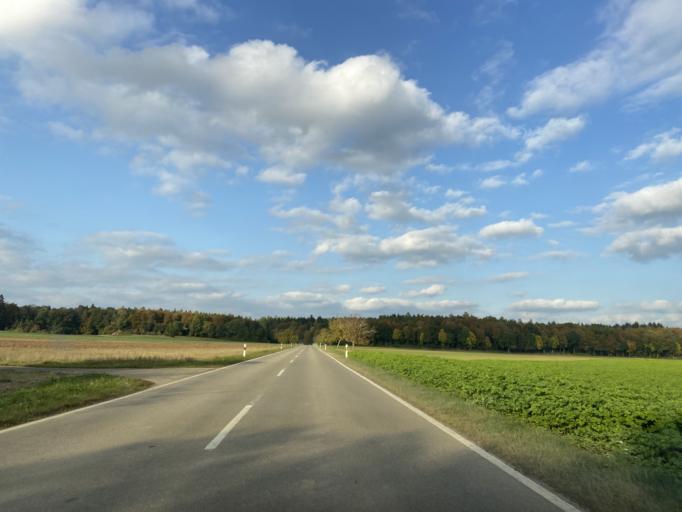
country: DE
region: Baden-Wuerttemberg
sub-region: Tuebingen Region
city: Scheer
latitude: 48.0984
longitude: 9.3343
